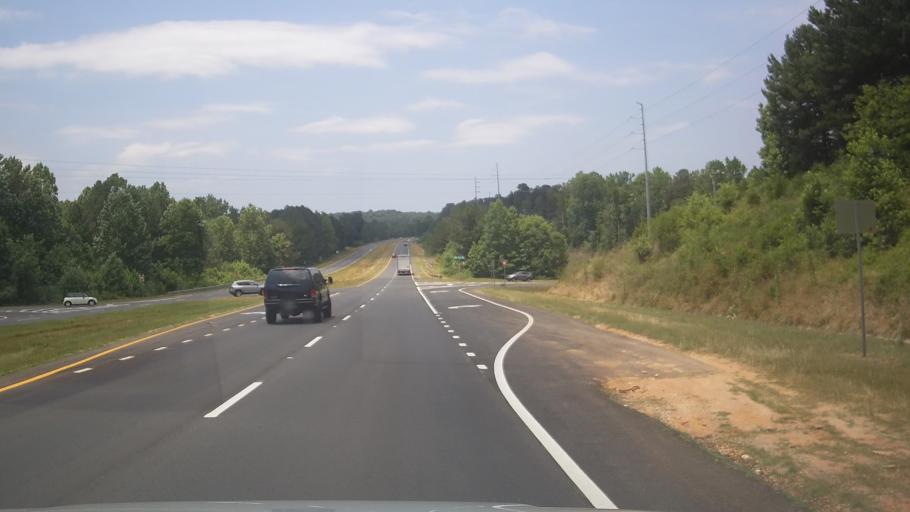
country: US
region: Georgia
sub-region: Jackson County
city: Commerce
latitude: 34.2175
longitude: -83.4447
